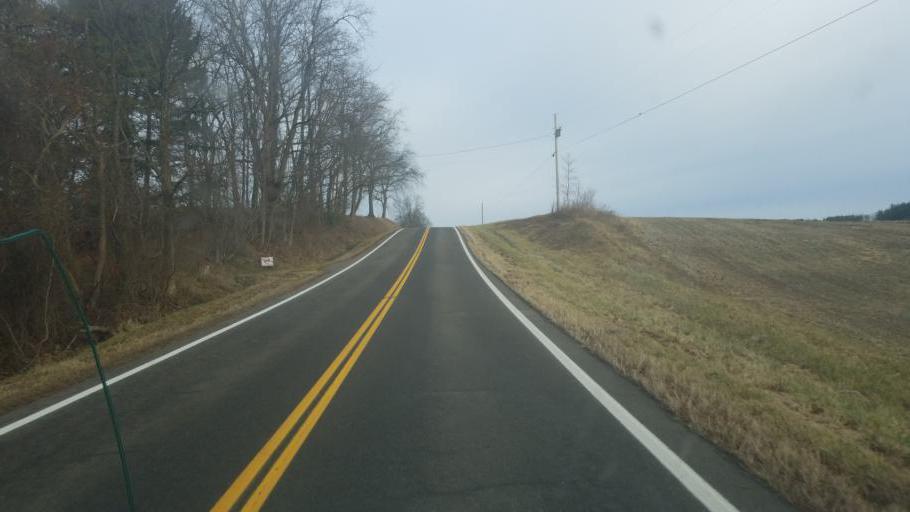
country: US
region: Ohio
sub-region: Sandusky County
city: Bellville
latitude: 40.6536
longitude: -82.3771
